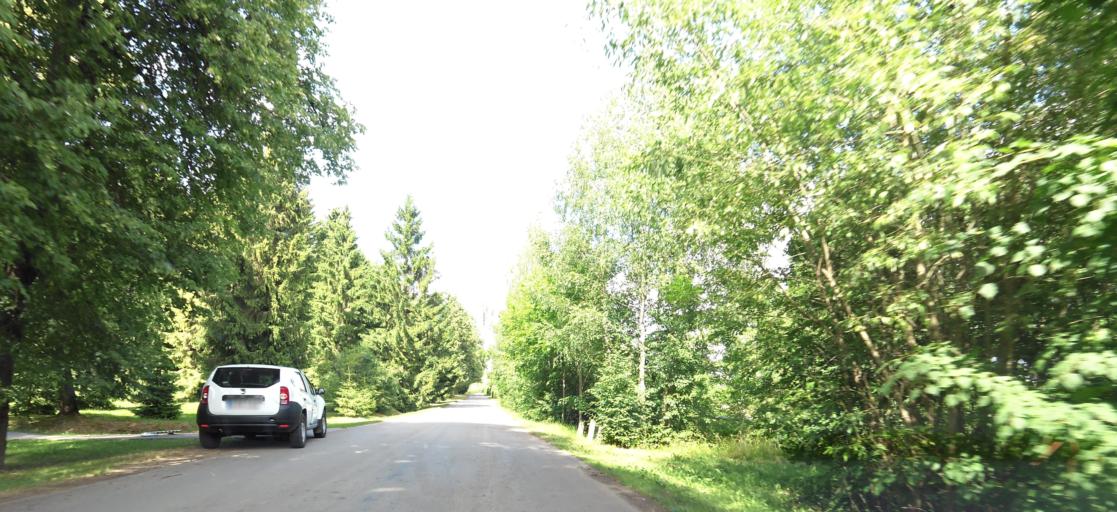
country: LT
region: Panevezys
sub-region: Birzai
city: Birzai
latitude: 56.1989
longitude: 24.6276
